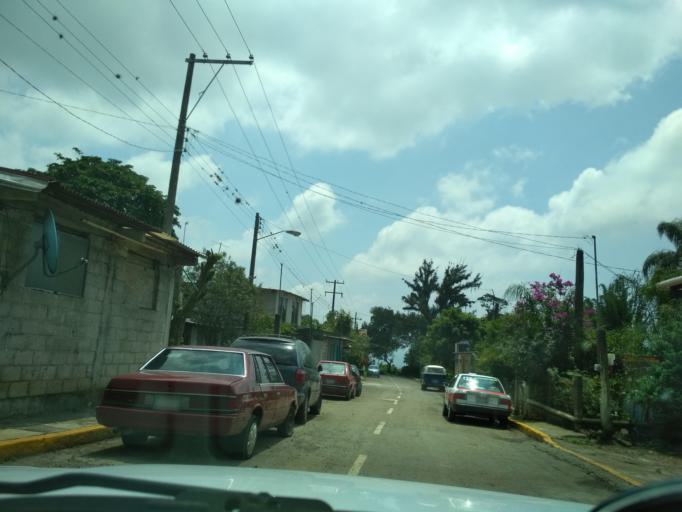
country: MX
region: Veracruz
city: Ixtac Zoquitlan
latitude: 18.8764
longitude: -97.0767
